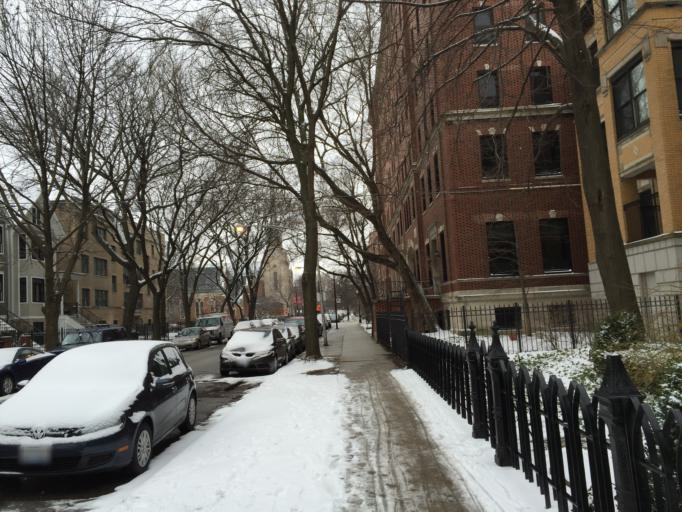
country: US
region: Illinois
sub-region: Cook County
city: Chicago
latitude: 41.9264
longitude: -87.6465
